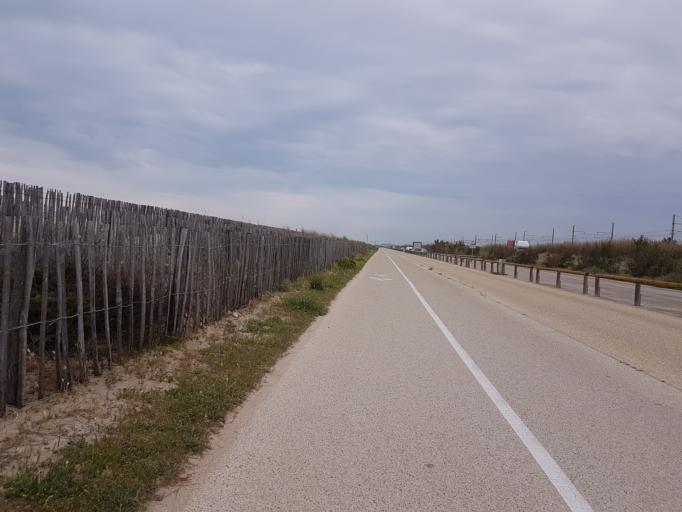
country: FR
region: Languedoc-Roussillon
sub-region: Departement de l'Herault
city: Sete
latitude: 43.3835
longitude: 3.6417
